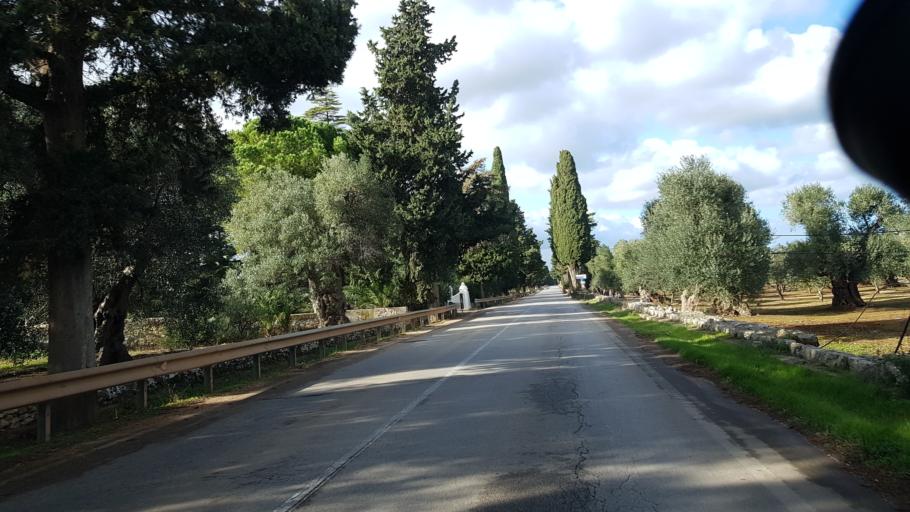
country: IT
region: Apulia
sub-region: Provincia di Brindisi
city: Montalbano
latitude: 40.7586
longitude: 17.5332
